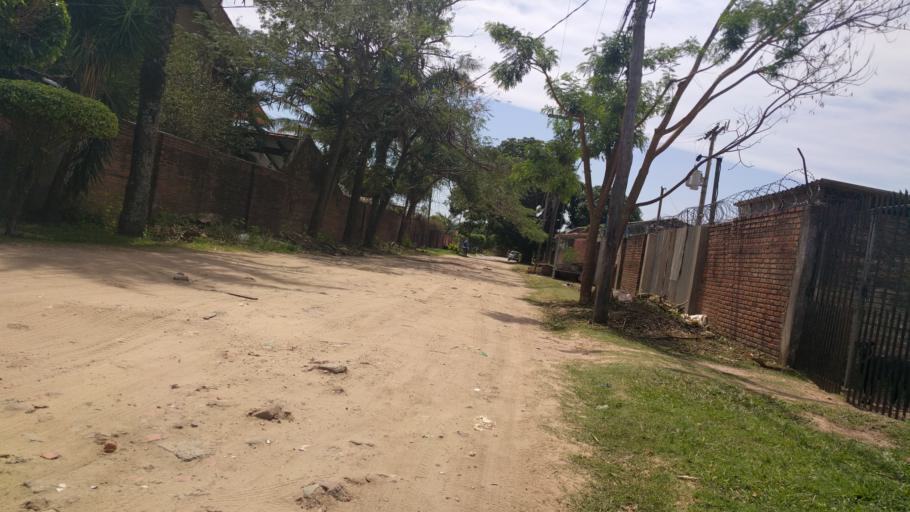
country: BO
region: Santa Cruz
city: Santa Cruz de la Sierra
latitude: -17.8190
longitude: -63.2210
